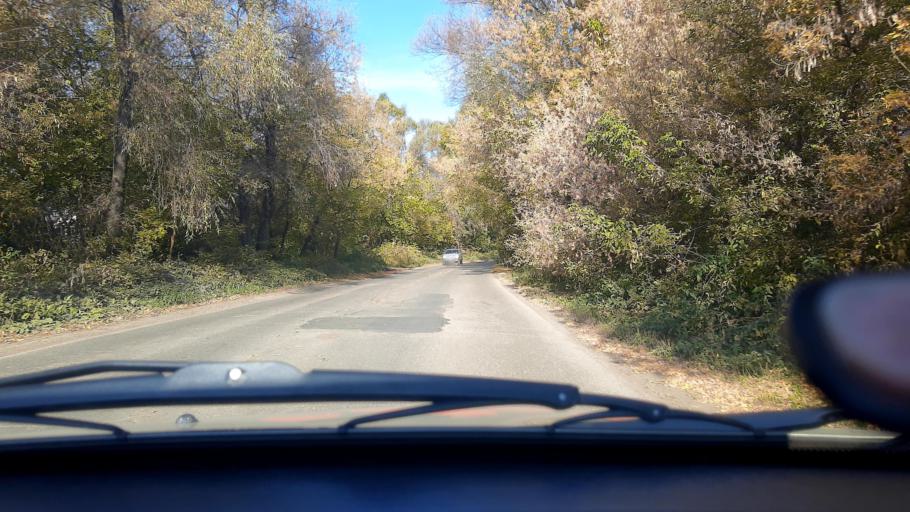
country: RU
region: Bashkortostan
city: Ufa
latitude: 54.8028
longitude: 56.1515
